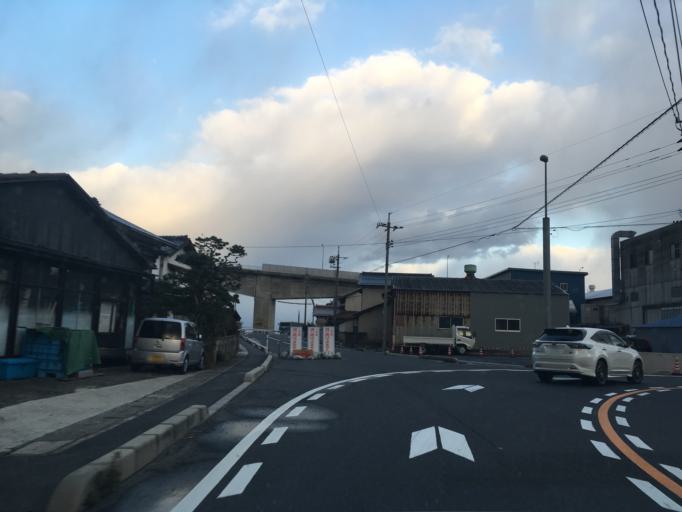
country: JP
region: Shimane
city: Matsue-shi
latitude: 35.4502
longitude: 133.1242
